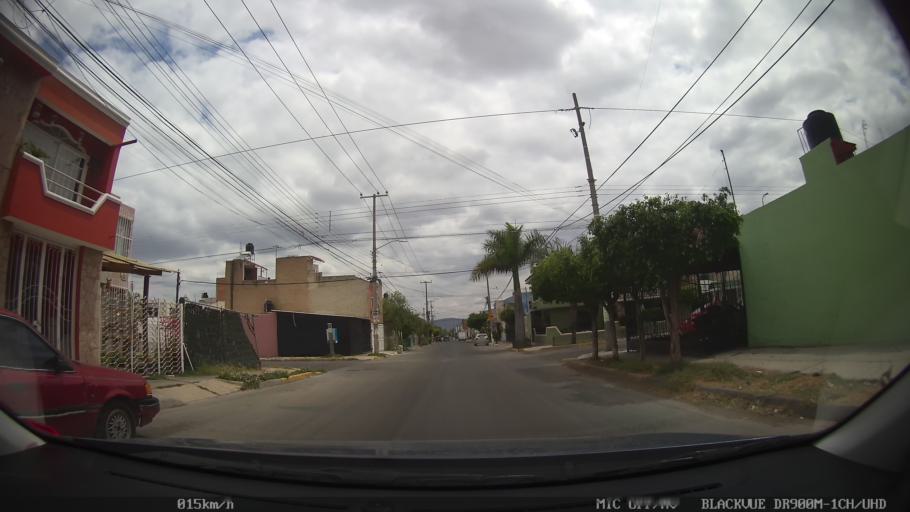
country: MX
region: Jalisco
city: Tonala
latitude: 20.6383
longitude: -103.2528
